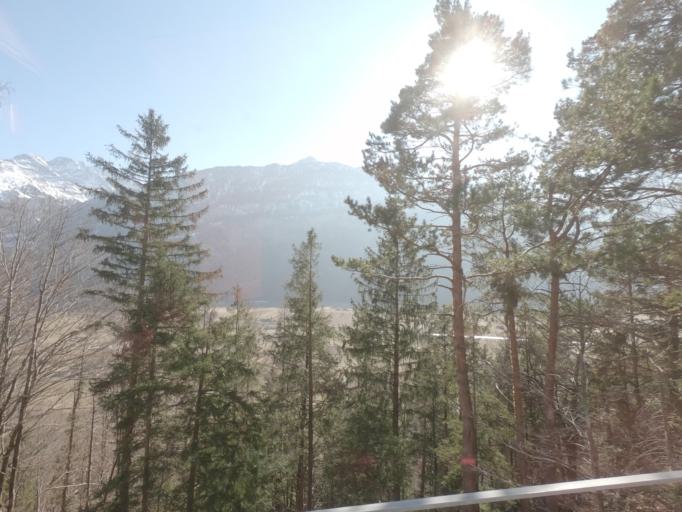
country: CH
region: Bern
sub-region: Interlaken-Oberhasli District
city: Meiringen
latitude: 46.7437
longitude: 8.1607
